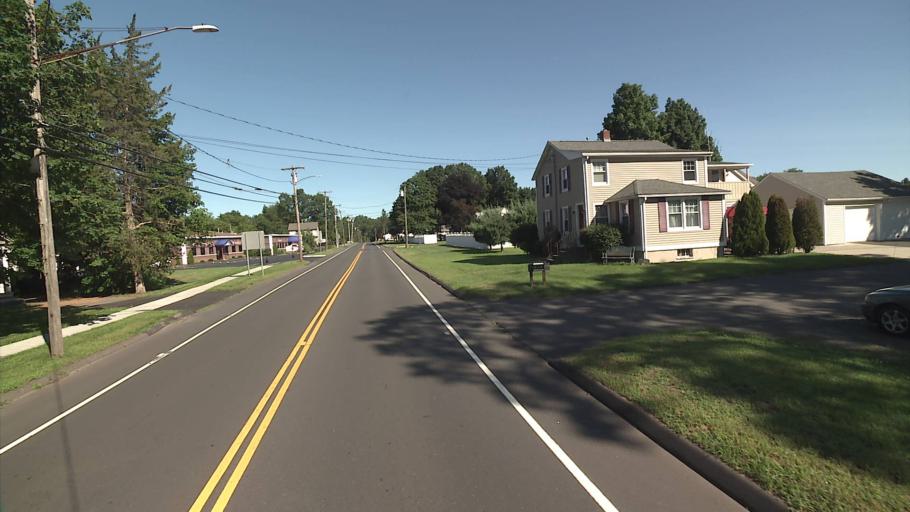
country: US
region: Connecticut
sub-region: New Haven County
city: Cheshire Village
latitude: 41.5665
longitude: -72.8926
